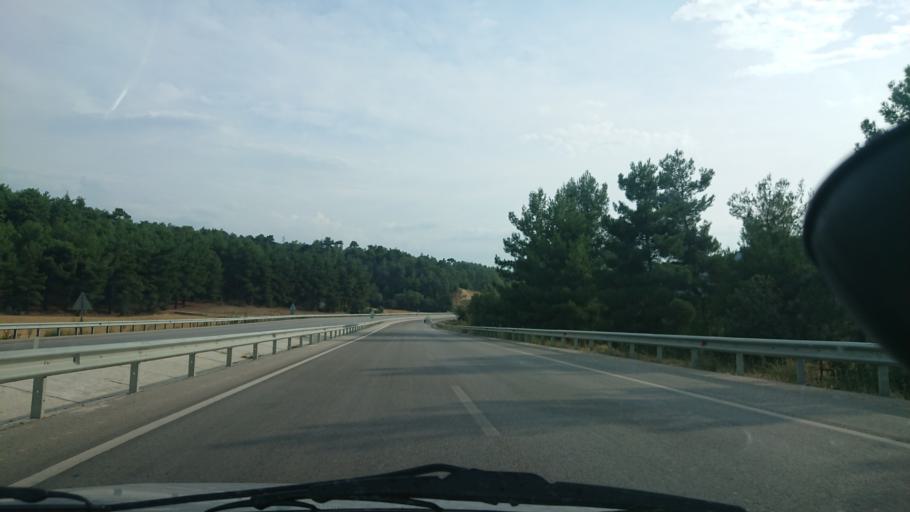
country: TR
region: Kuetahya
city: Gediz
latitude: 38.9184
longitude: 29.3022
